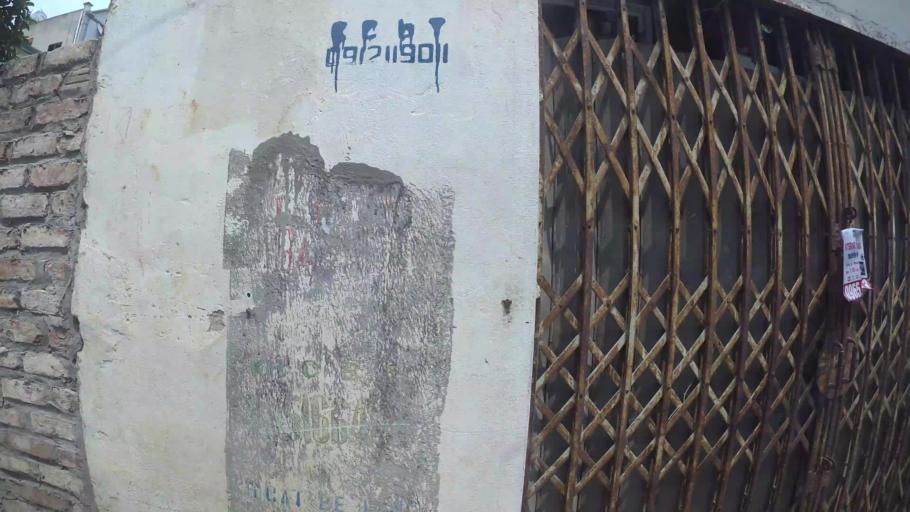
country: VN
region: Ha Noi
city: Tay Ho
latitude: 21.0875
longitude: 105.8028
